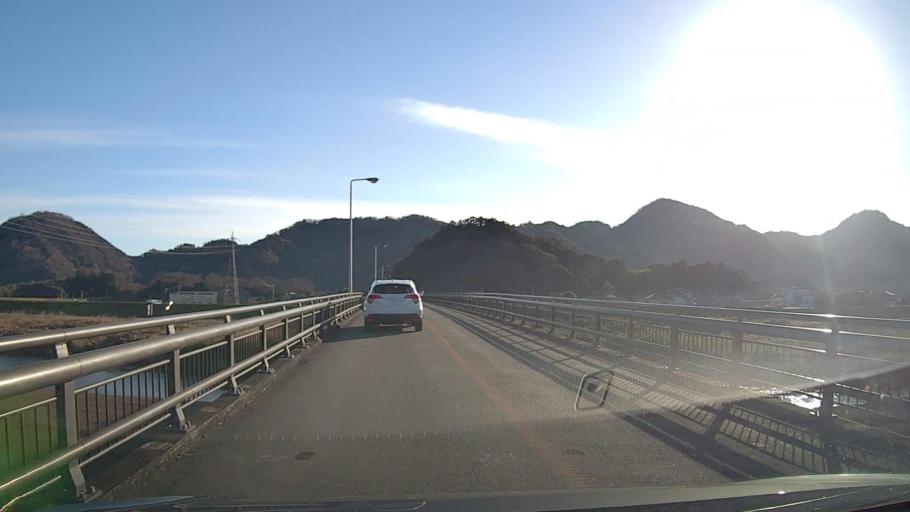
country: JP
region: Shizuoka
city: Mishima
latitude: 35.0764
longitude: 138.9191
